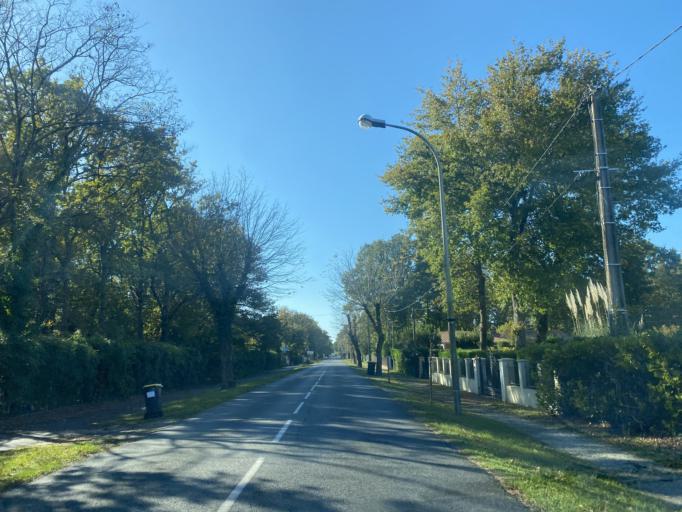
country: FR
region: Aquitaine
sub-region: Departement de la Gironde
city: Hourtin
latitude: 45.1822
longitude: -1.0765
